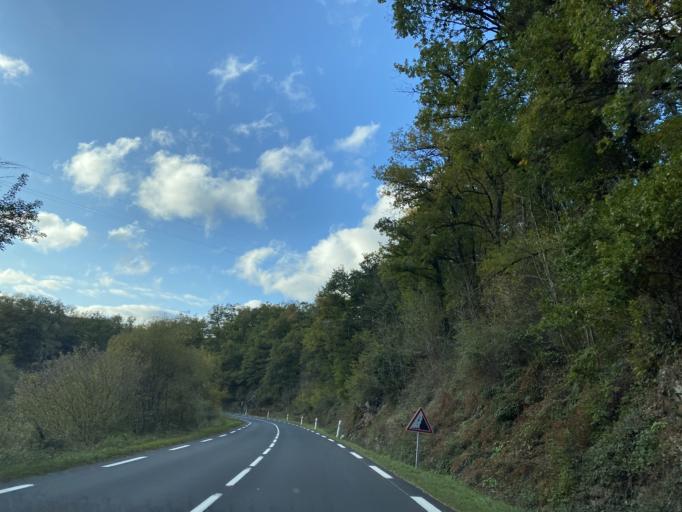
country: FR
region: Auvergne
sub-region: Departement du Puy-de-Dome
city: Job
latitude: 45.6491
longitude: 3.6776
